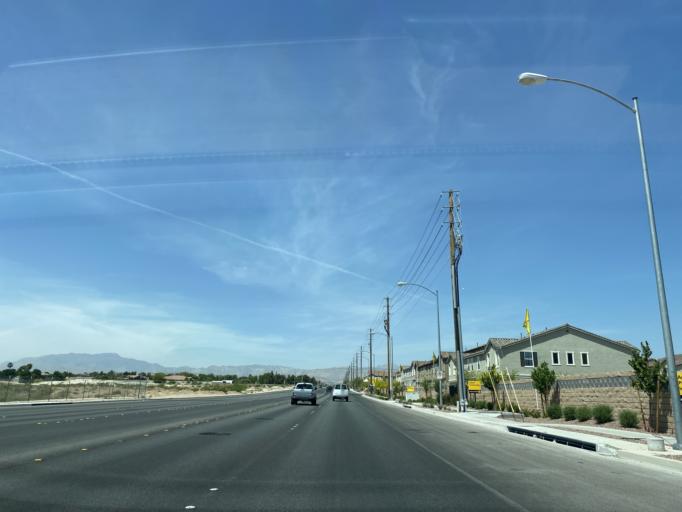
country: US
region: Nevada
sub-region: Clark County
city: Spring Valley
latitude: 36.0861
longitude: -115.2125
